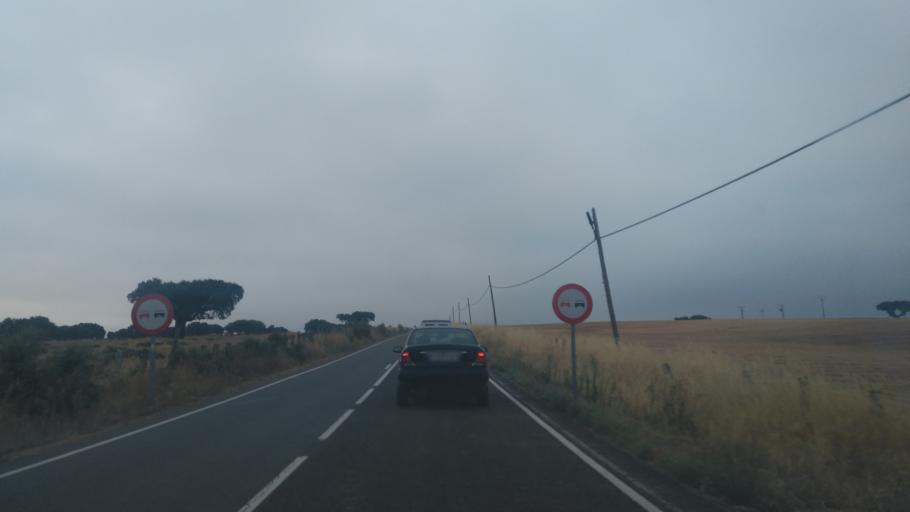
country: ES
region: Castille and Leon
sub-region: Provincia de Salamanca
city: Robliza de Cojos
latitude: 40.8566
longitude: -5.9620
